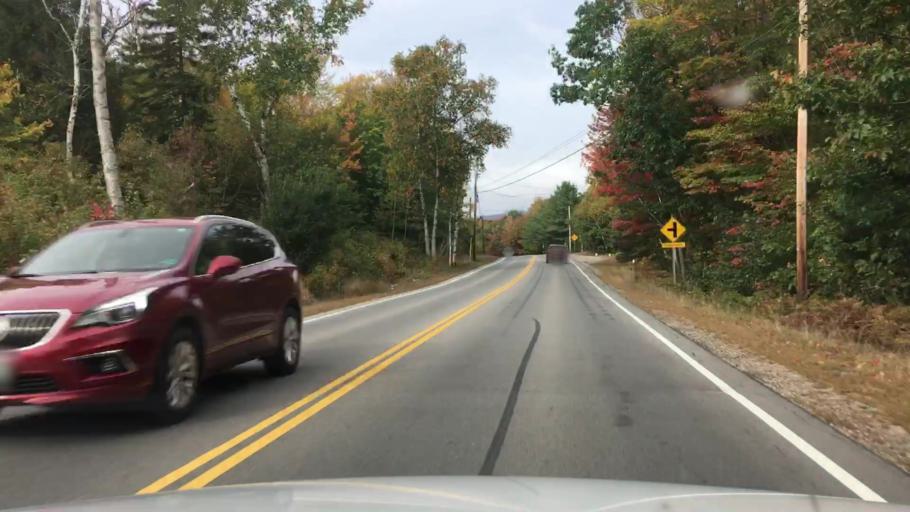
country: US
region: New Hampshire
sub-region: Coos County
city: Gorham
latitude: 44.3873
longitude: -71.1356
